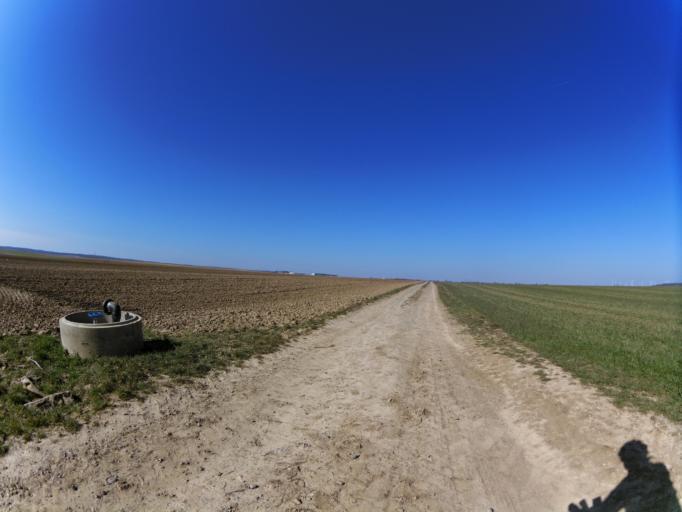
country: DE
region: Bavaria
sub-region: Regierungsbezirk Unterfranken
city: Oberpleichfeld
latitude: 49.8784
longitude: 10.0702
